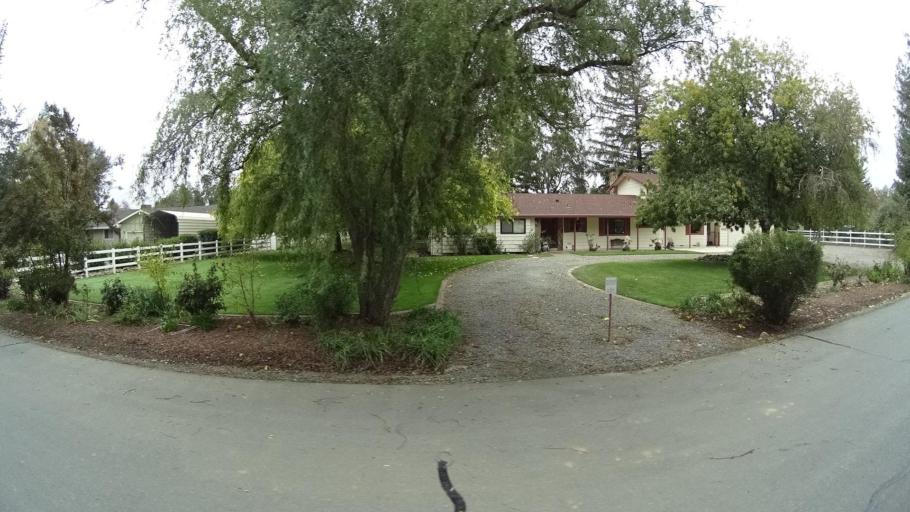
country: US
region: California
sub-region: Sacramento County
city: Wilton
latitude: 38.4337
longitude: -121.3005
